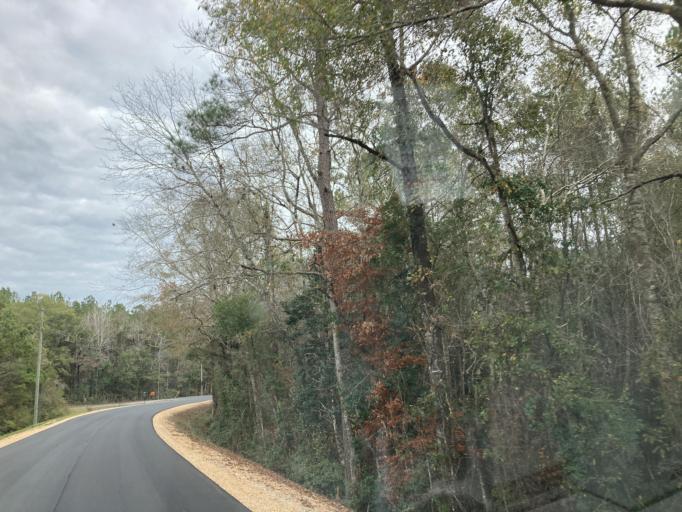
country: US
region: Mississippi
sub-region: Perry County
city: New Augusta
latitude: 31.0683
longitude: -89.1609
